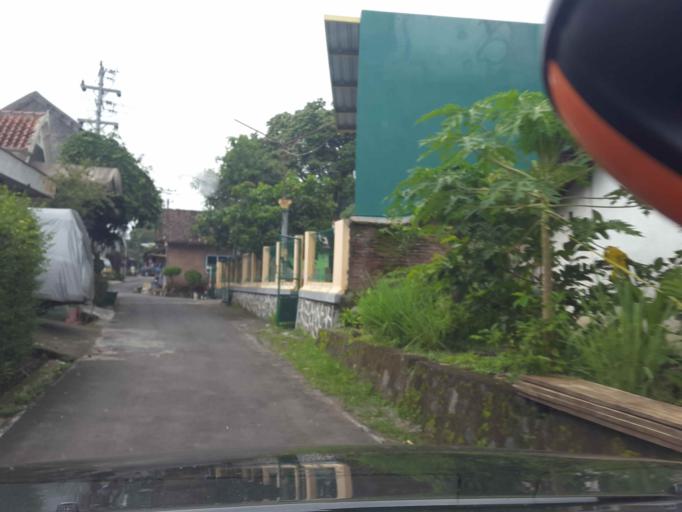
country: ID
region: Central Java
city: Salatiga
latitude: -7.3370
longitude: 110.5118
